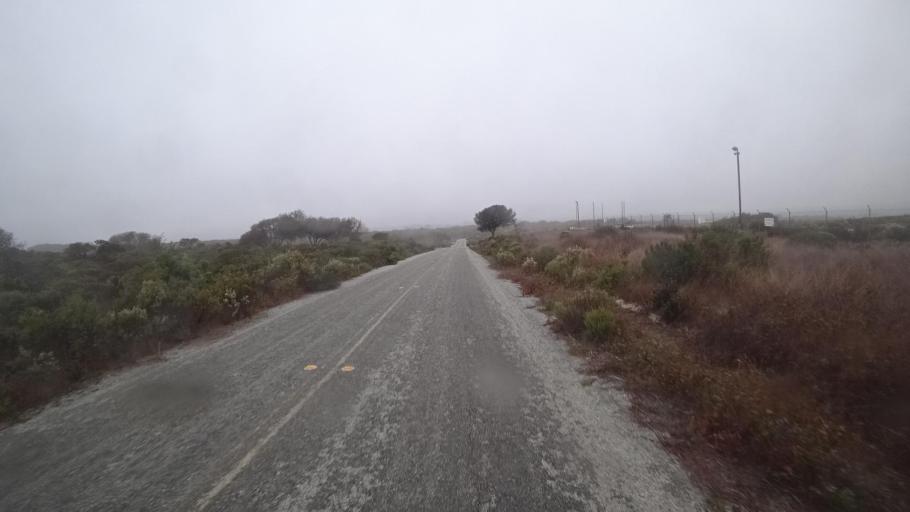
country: US
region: California
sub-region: Monterey County
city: Marina
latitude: 36.6382
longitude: -121.7353
